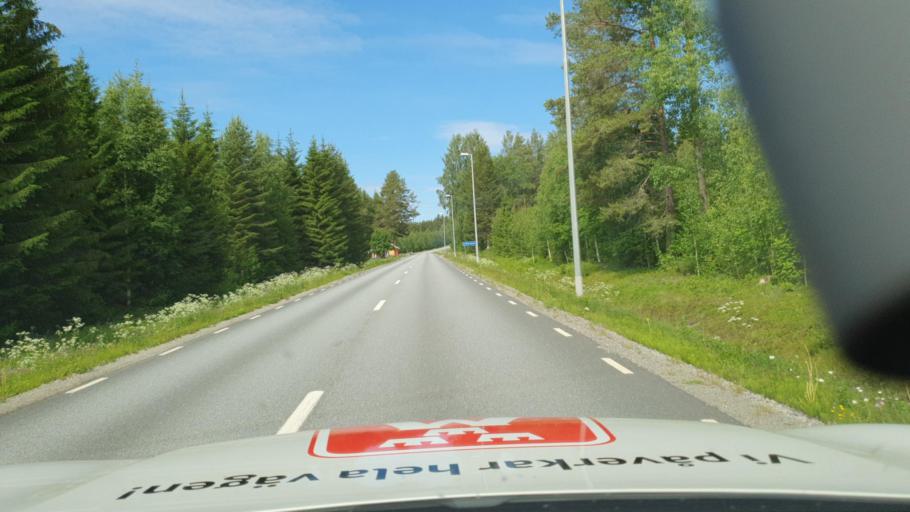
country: SE
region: Vaesterbotten
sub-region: Skelleftea Kommun
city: Forsbacka
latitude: 64.7080
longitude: 20.4332
